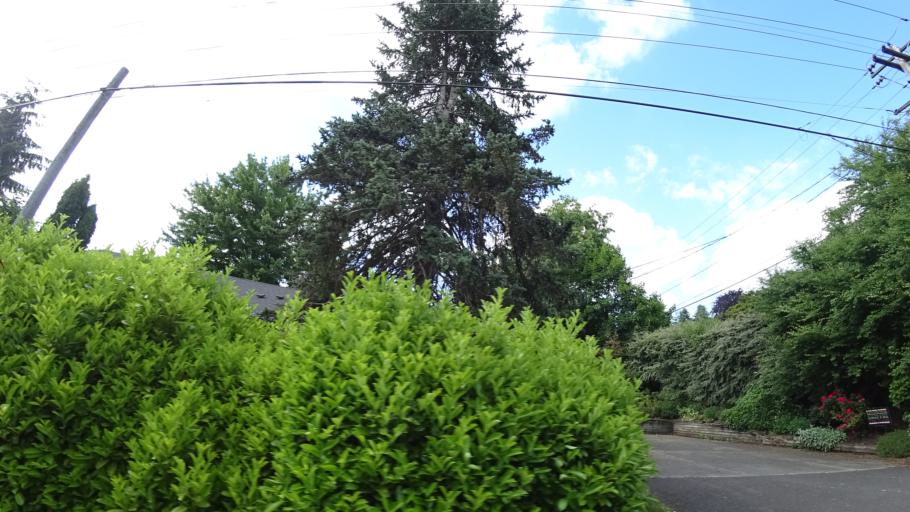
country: US
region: Oregon
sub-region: Washington County
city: Garden Home-Whitford
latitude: 45.4725
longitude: -122.7110
